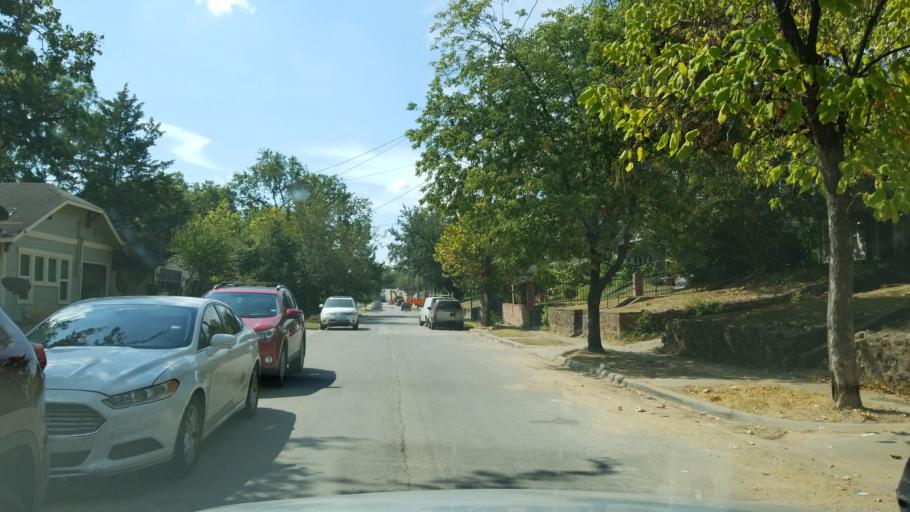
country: US
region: Texas
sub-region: Dallas County
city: Dallas
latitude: 32.7532
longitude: -96.8218
